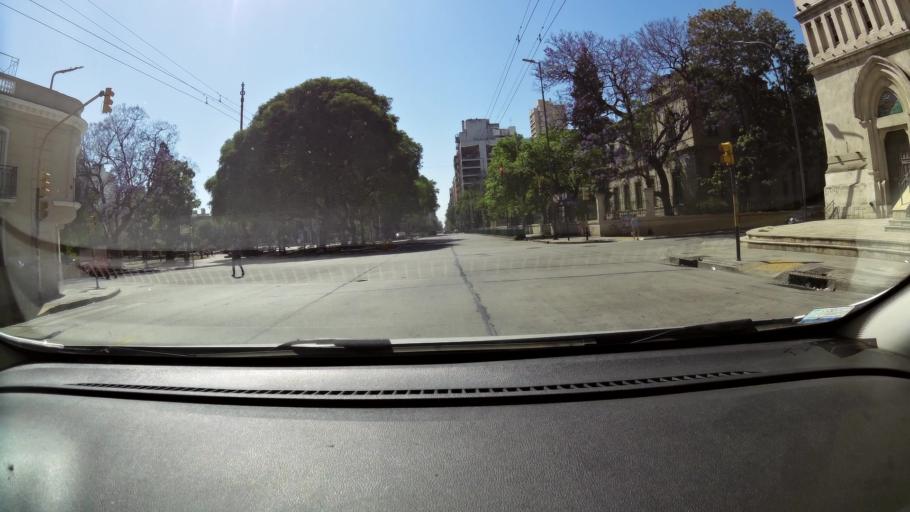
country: AR
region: Cordoba
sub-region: Departamento de Capital
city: Cordoba
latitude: -31.4096
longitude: -64.1968
